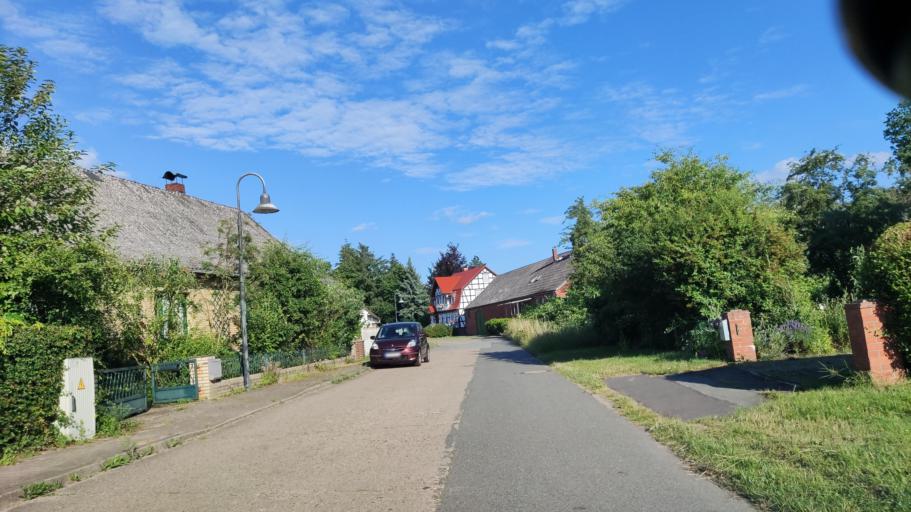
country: DE
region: Brandenburg
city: Lanz
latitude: 53.0384
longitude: 11.5598
